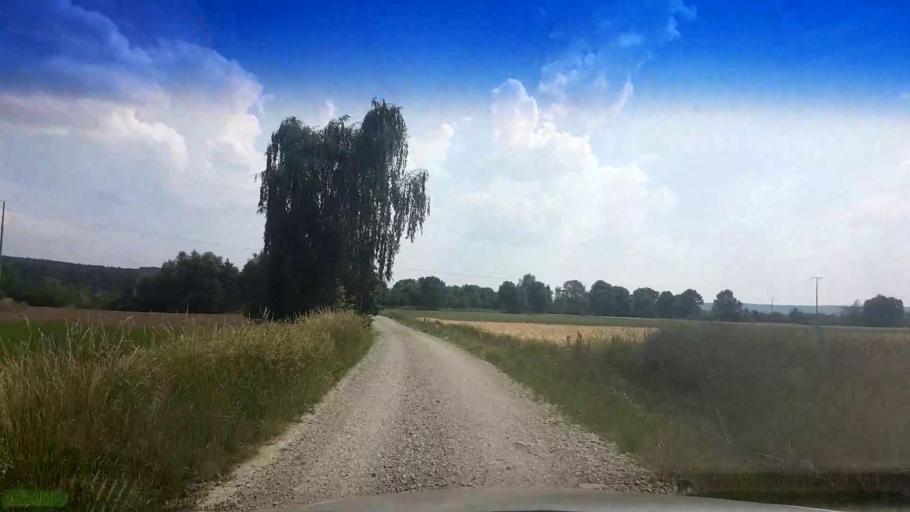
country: DE
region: Bavaria
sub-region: Upper Franconia
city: Rattelsdorf
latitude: 50.0047
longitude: 10.9035
